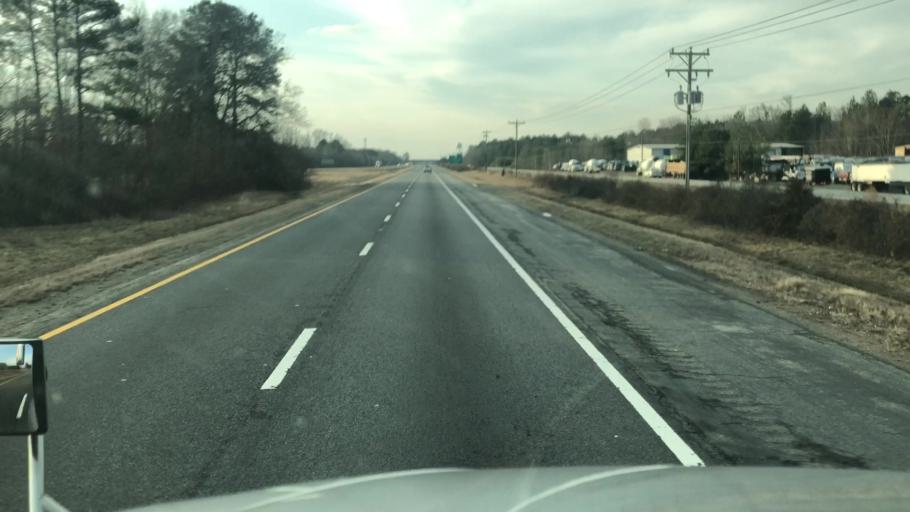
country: US
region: Virginia
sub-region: Sussex County
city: Sussex
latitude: 36.9624
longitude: -77.3926
